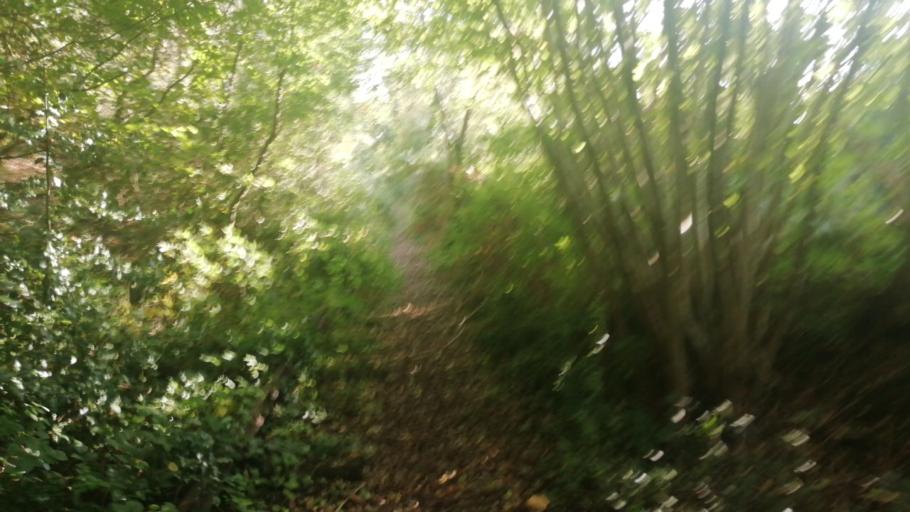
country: FR
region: Haute-Normandie
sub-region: Departement de la Seine-Maritime
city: Rolleville
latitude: 49.5892
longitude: 0.2120
